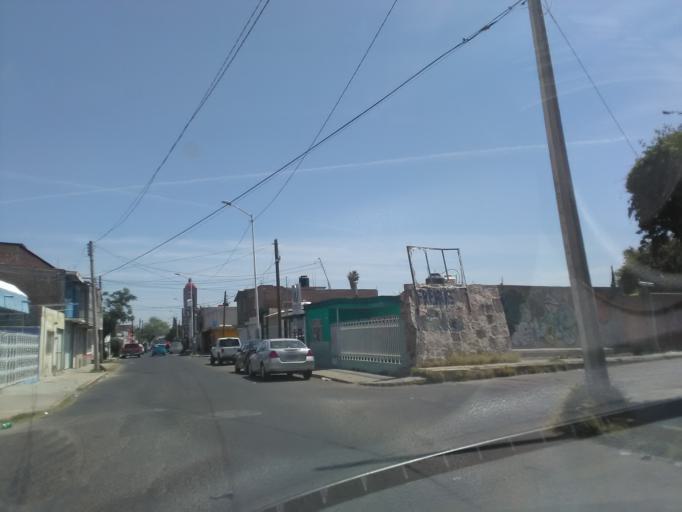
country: MX
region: Durango
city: Victoria de Durango
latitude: 24.0111
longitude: -104.6603
